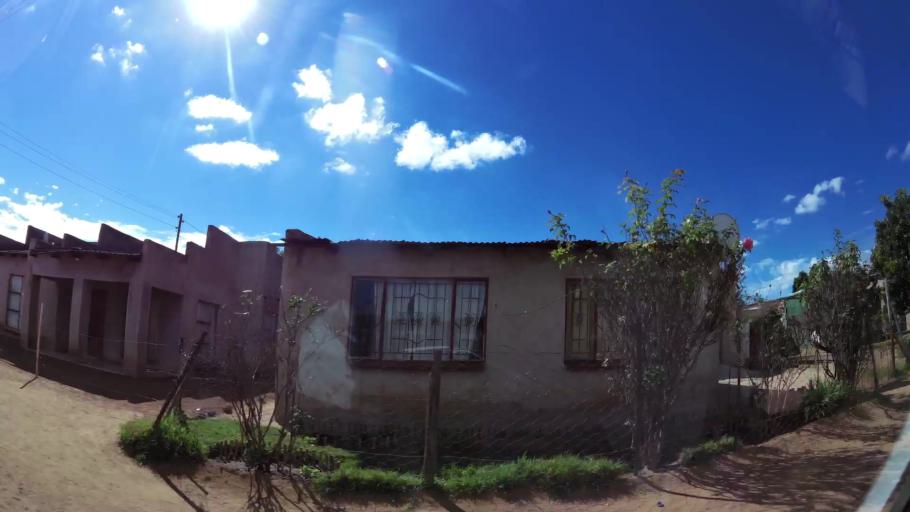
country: ZA
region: Limpopo
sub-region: Waterberg District Municipality
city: Bela-Bela
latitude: -24.8787
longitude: 28.3266
